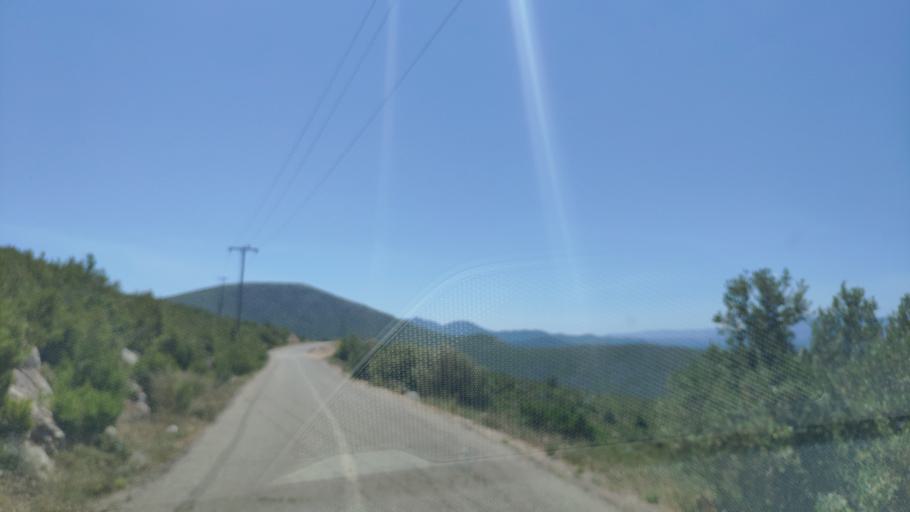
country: GR
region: Central Greece
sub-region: Nomos Voiotias
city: Kaparellion
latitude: 38.1951
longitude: 23.1470
